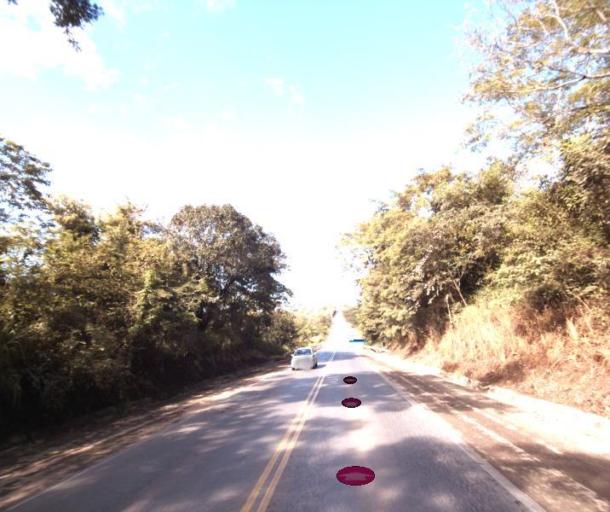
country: BR
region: Goias
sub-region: Itapaci
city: Itapaci
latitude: -14.8156
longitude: -49.2945
